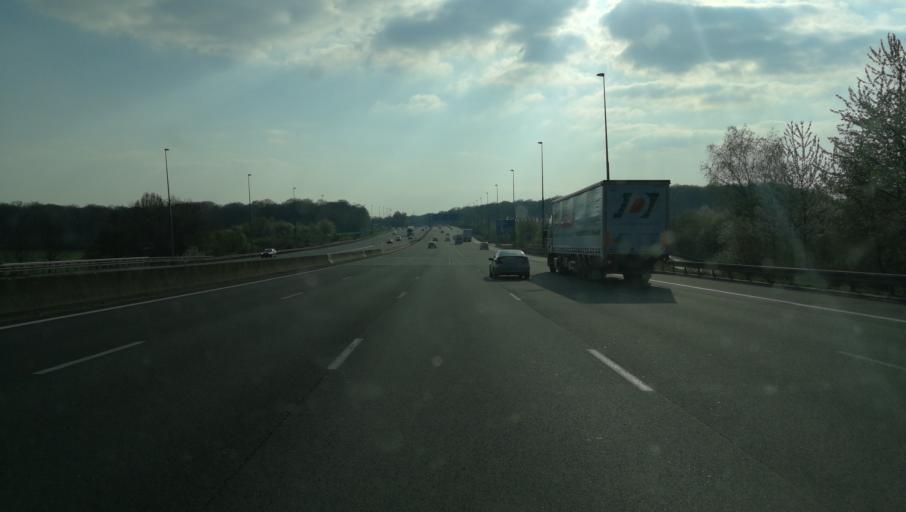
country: FR
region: Ile-de-France
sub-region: Departement des Yvelines
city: Saint-Arnoult-en-Yvelines
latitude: 48.5522
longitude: 1.9239
